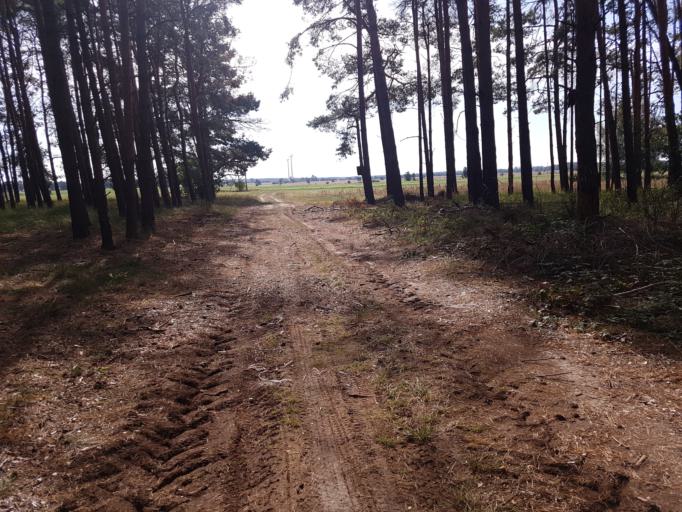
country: DE
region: Brandenburg
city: Schilda
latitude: 51.6411
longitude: 13.3333
